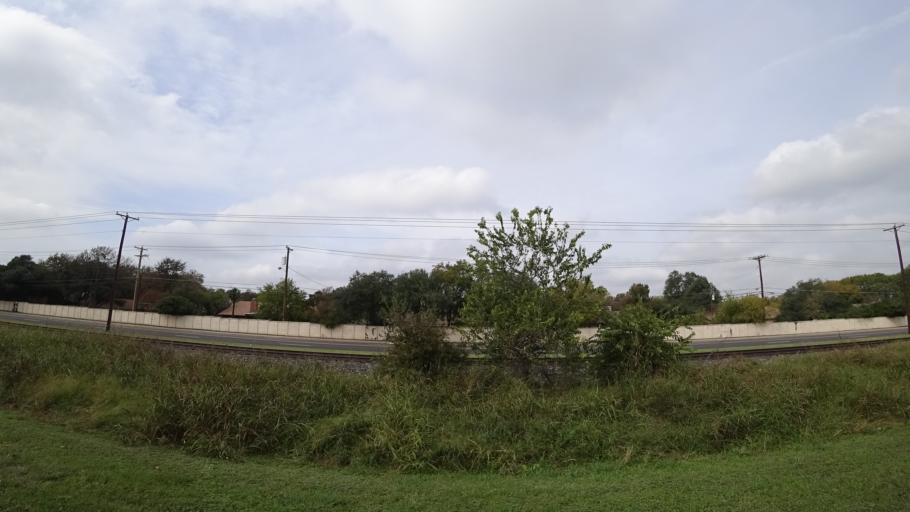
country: US
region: Texas
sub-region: Williamson County
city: Round Rock
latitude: 30.4963
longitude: -97.6889
